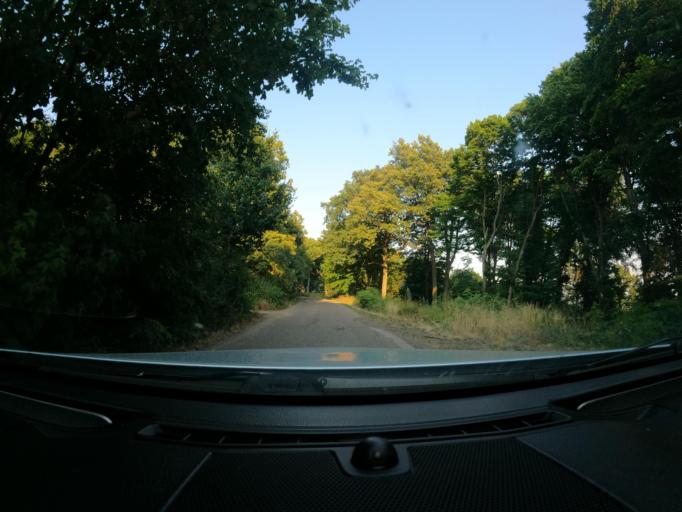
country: RS
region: Autonomna Pokrajina Vojvodina
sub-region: Juznobacki Okrug
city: Beocin
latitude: 45.1566
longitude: 19.7371
